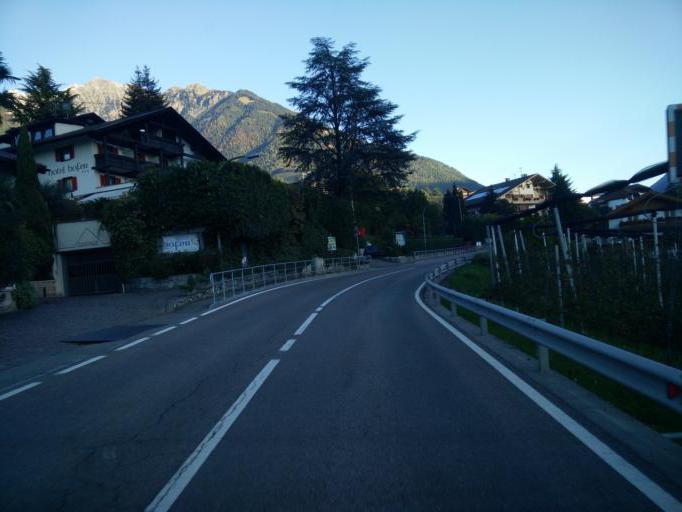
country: IT
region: Trentino-Alto Adige
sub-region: Bolzano
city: Caines
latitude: 46.6858
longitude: 11.1672
